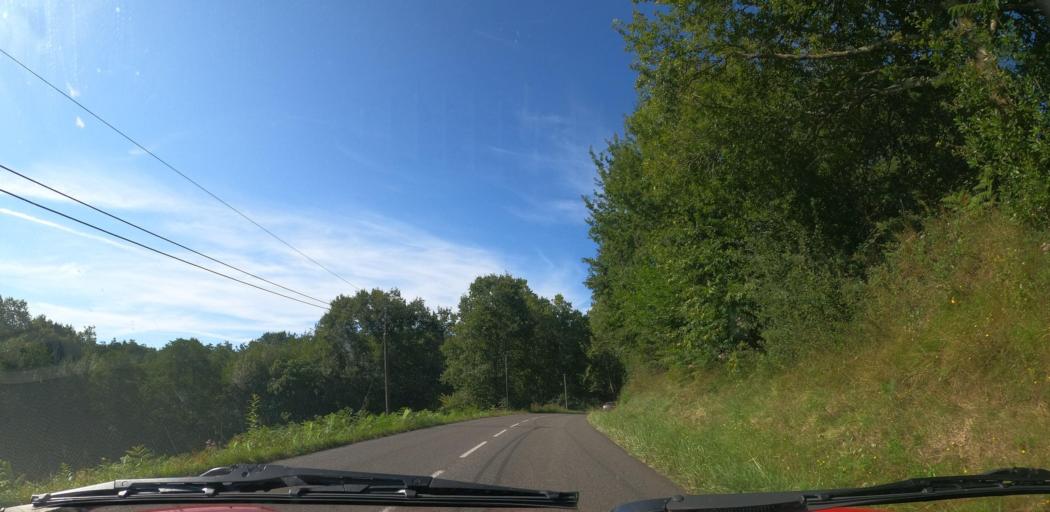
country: FR
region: Aquitaine
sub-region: Departement des Pyrenees-Atlantiques
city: Saint-Pee-sur-Nivelle
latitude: 43.3706
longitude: -1.5457
